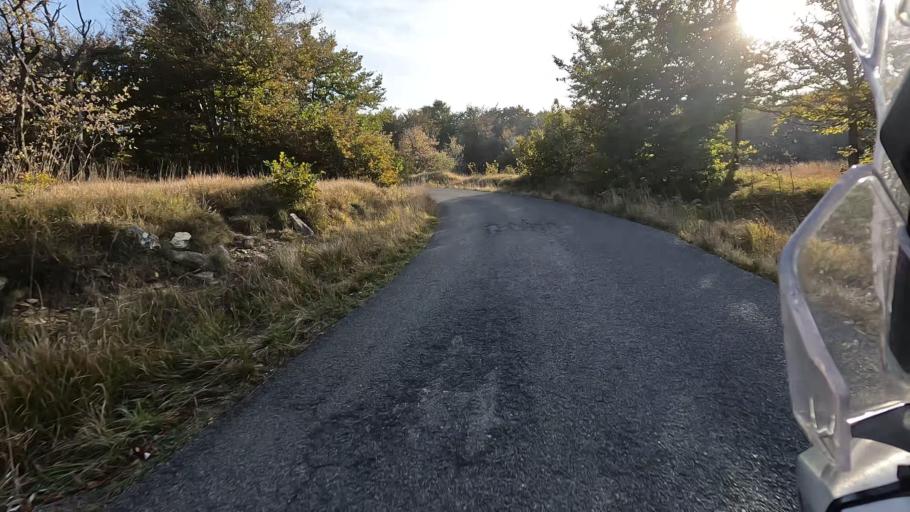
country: IT
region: Liguria
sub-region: Provincia di Genova
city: Sciarborasca
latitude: 44.4320
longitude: 8.5865
